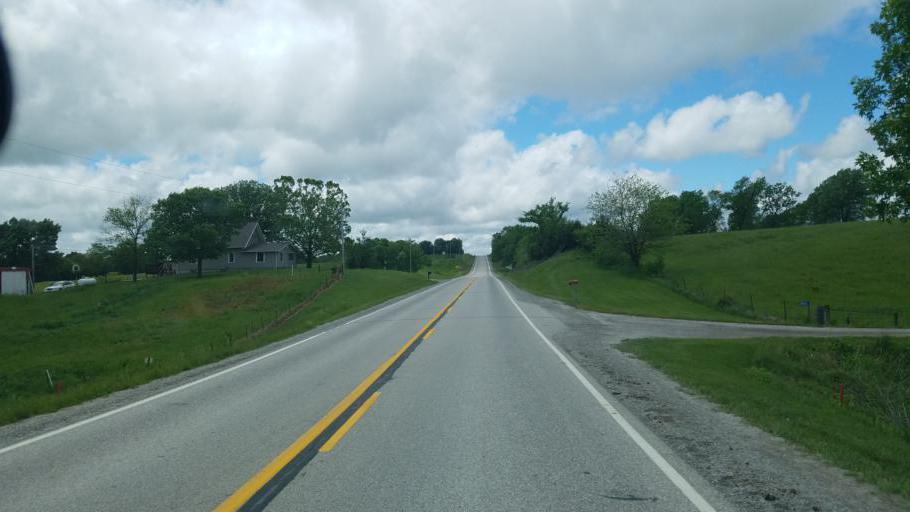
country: US
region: Iowa
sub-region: Decatur County
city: Lamoni
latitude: 40.6238
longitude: -93.8576
